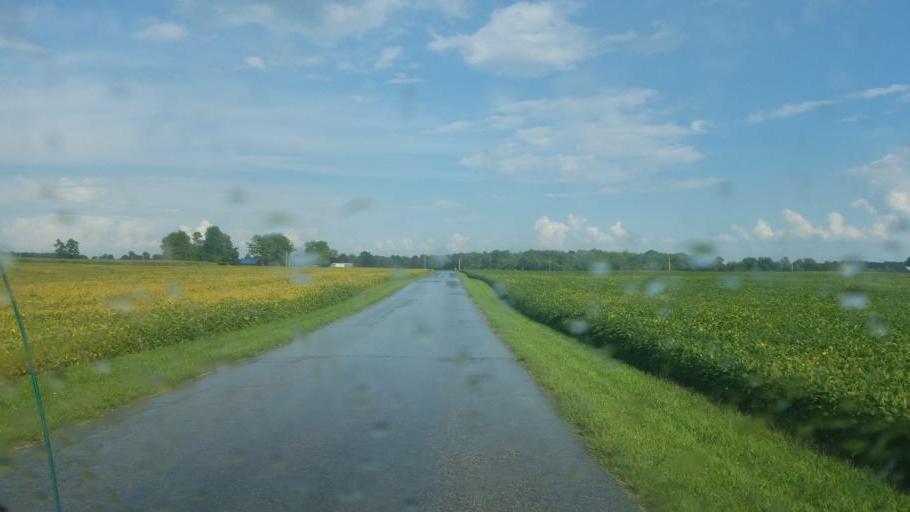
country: US
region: Ohio
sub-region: Huron County
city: Greenwich
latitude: 41.0076
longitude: -82.5881
